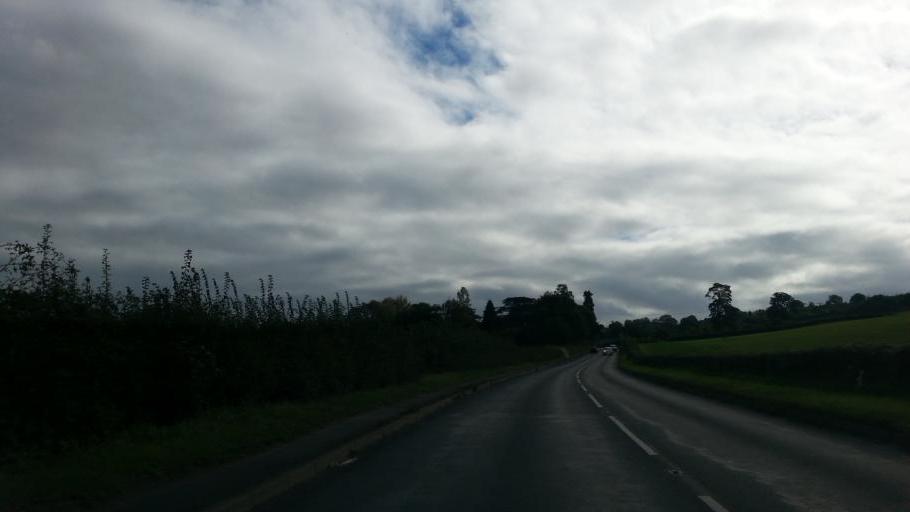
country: GB
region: England
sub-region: Herefordshire
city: Ross on Wye
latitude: 51.9115
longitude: -2.5486
